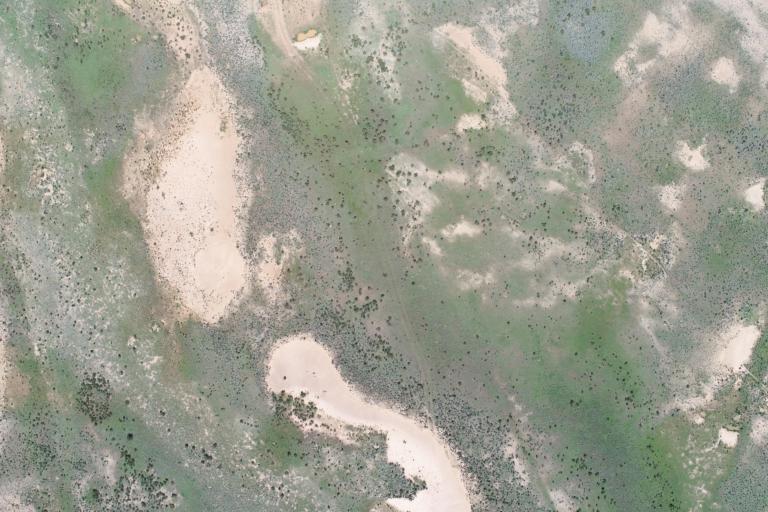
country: BO
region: La Paz
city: Curahuara de Carangas
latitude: -17.2965
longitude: -68.5226
